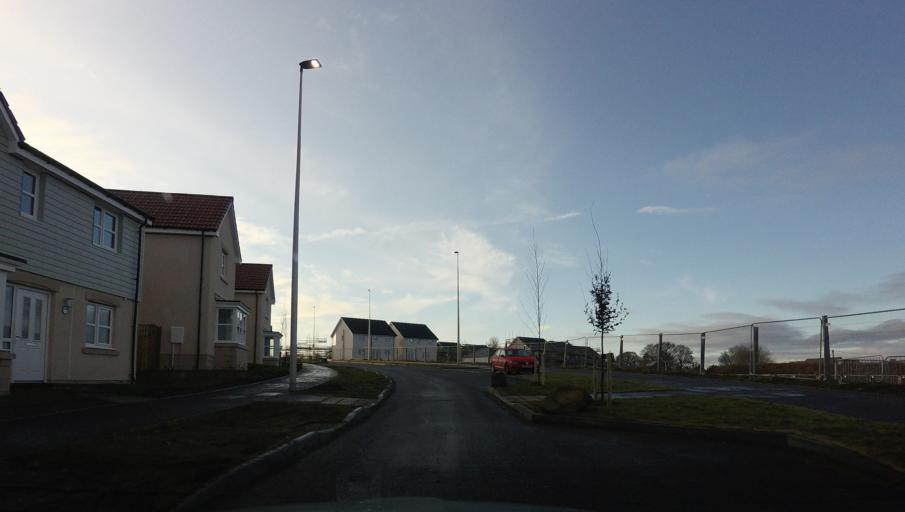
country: GB
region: Scotland
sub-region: West Lothian
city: East Calder
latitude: 55.9001
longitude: -3.4435
